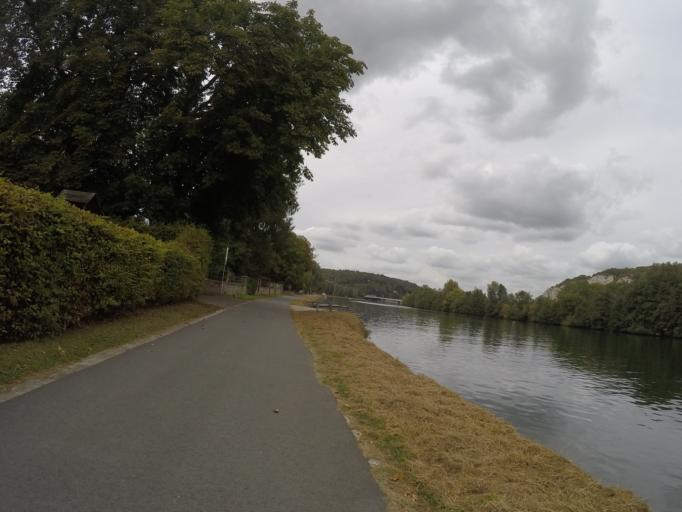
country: BE
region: Wallonia
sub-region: Province de Namur
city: Anhee
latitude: 50.3093
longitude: 4.8845
